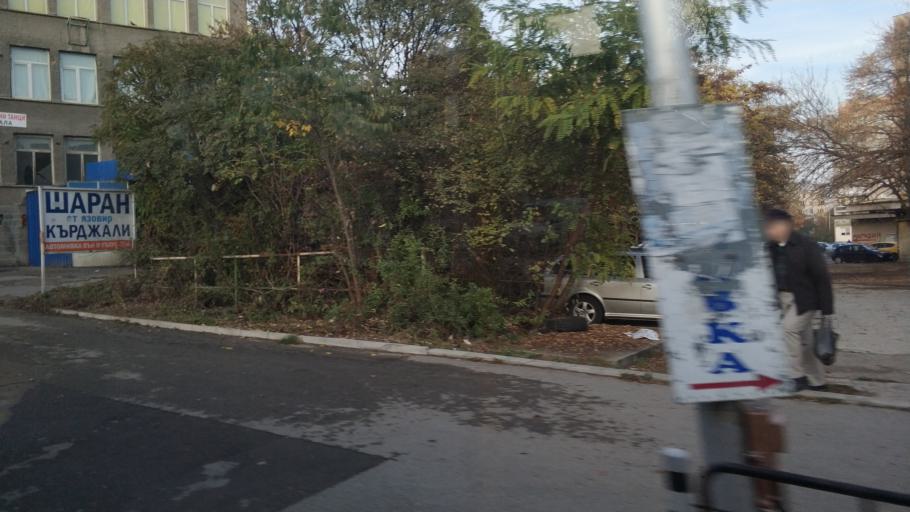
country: BG
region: Stara Zagora
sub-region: Obshtina Stara Zagora
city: Stara Zagora
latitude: 42.4187
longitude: 25.6208
